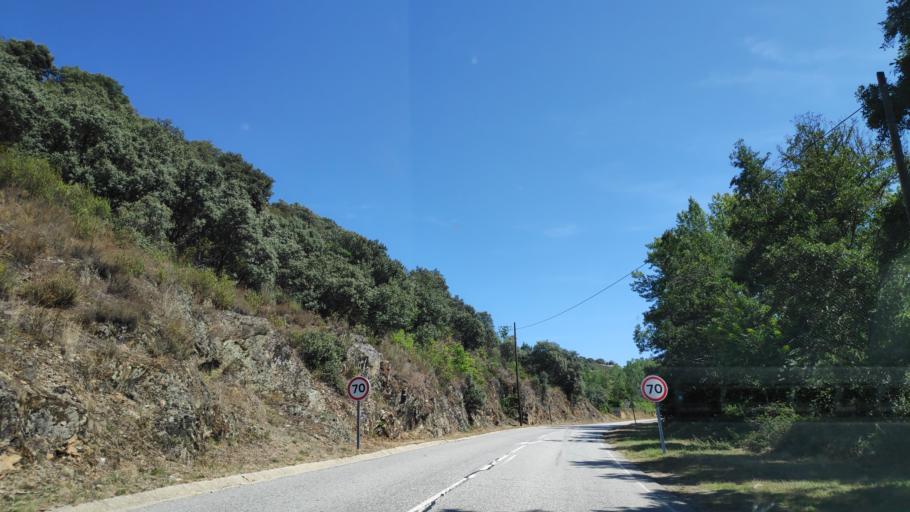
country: PT
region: Braganca
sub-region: Braganca Municipality
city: Braganca
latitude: 41.8606
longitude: -6.7472
